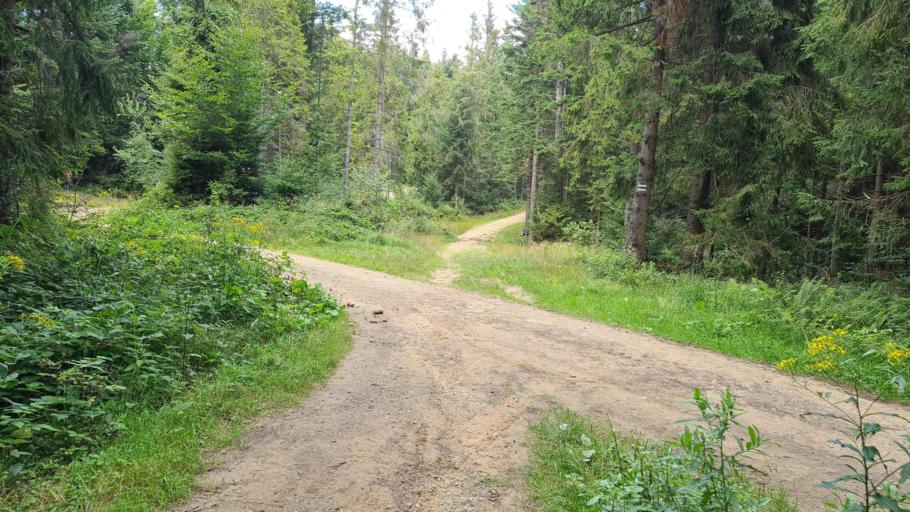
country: PL
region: Lesser Poland Voivodeship
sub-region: Powiat nowosadecki
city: Rytro
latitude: 49.4139
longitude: 20.6223
